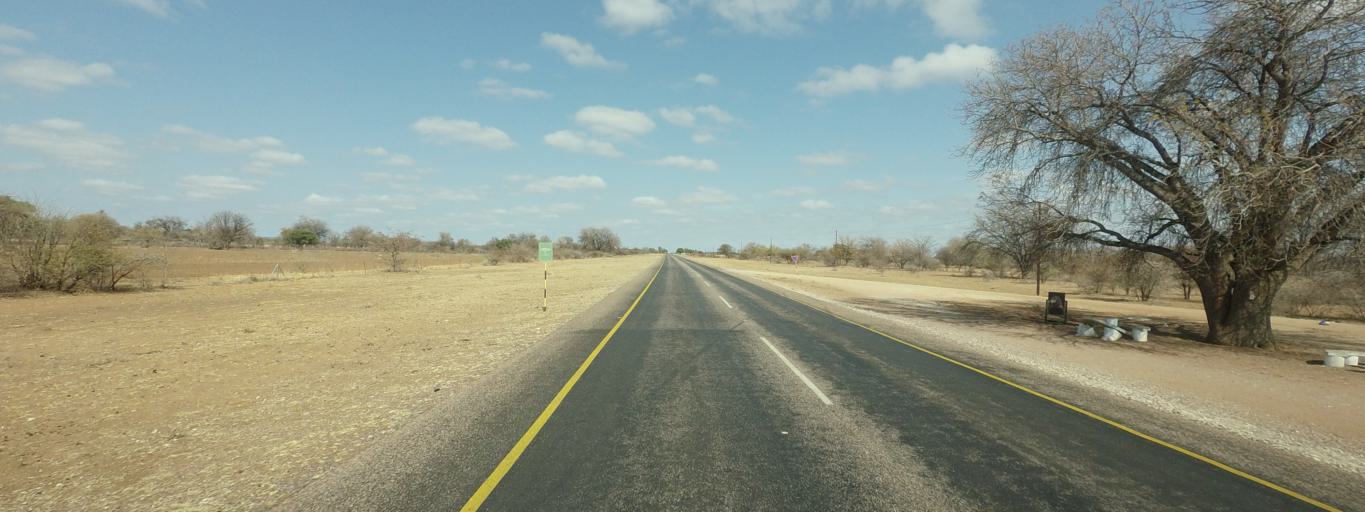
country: BW
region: Central
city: Ramokgonami
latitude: -22.8024
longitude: 27.5050
